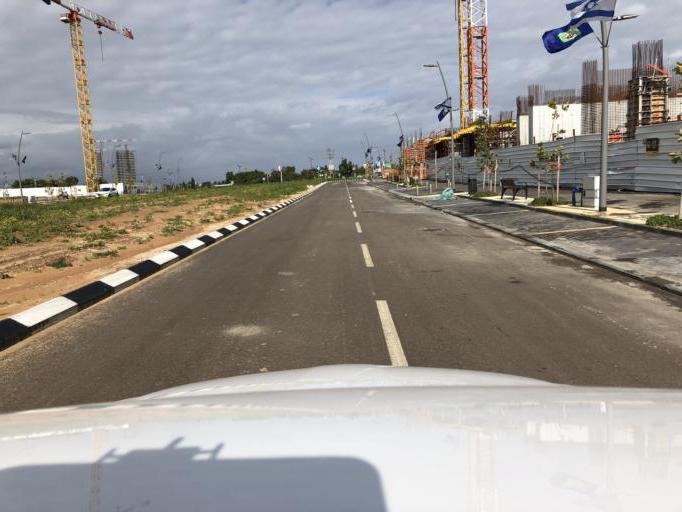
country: IL
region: Tel Aviv
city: Or Yehuda
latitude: 32.0494
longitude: 34.8403
